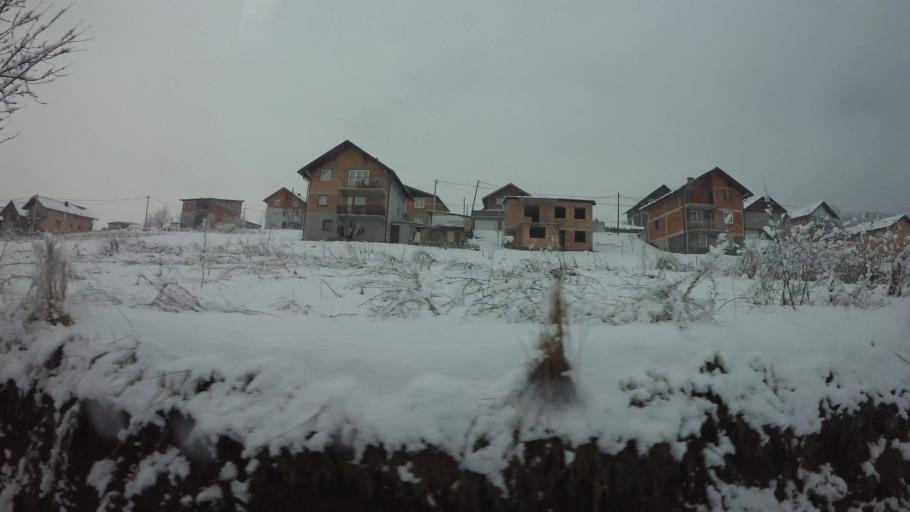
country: BA
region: Federation of Bosnia and Herzegovina
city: Vogosca
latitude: 43.8774
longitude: 18.3200
